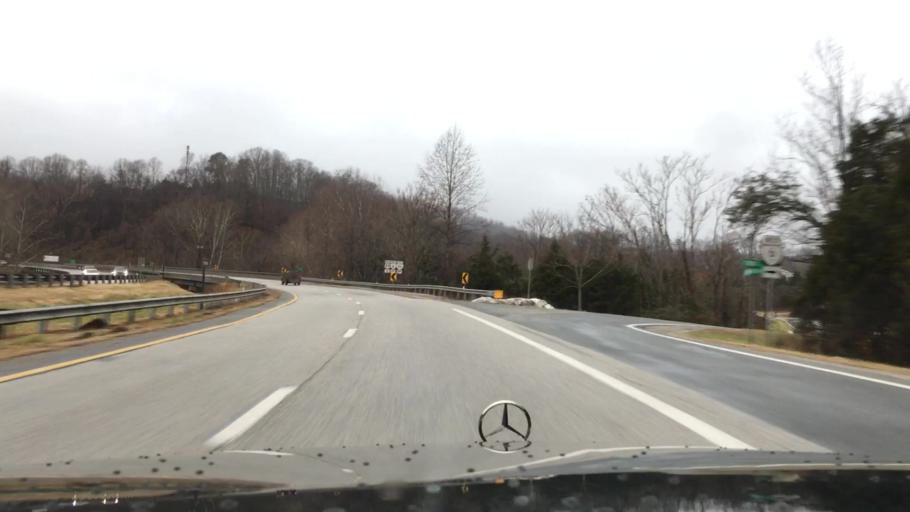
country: US
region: Virginia
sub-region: Nelson County
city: Nellysford
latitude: 37.8459
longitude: -78.8179
